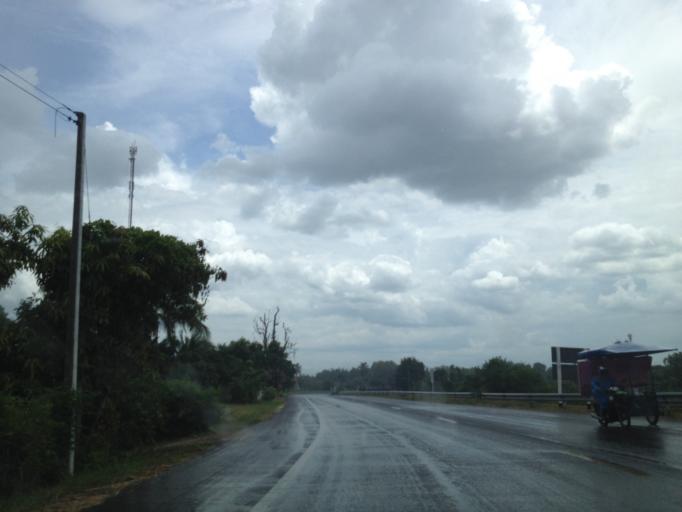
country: TH
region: Chiang Mai
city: San Pa Tong
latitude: 18.6400
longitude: 98.8463
